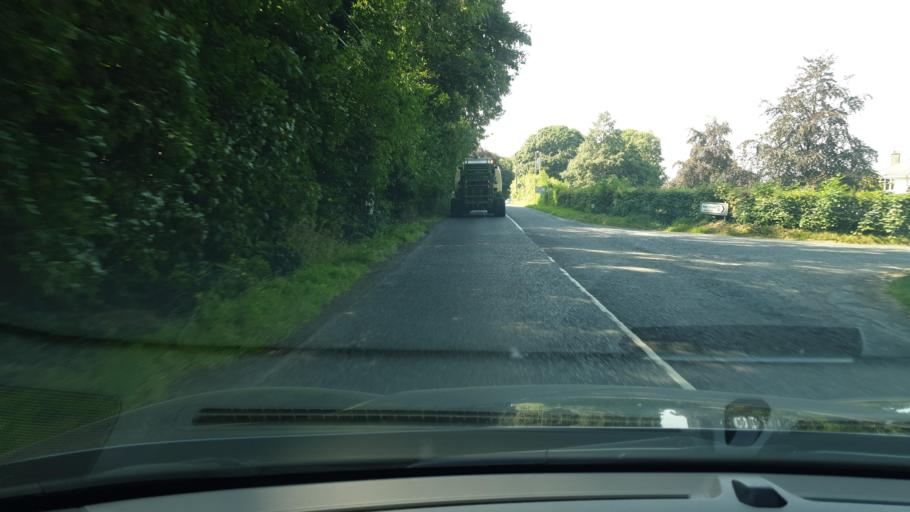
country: IE
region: Leinster
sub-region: An Mhi
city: Athboy
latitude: 53.6003
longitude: -6.8775
